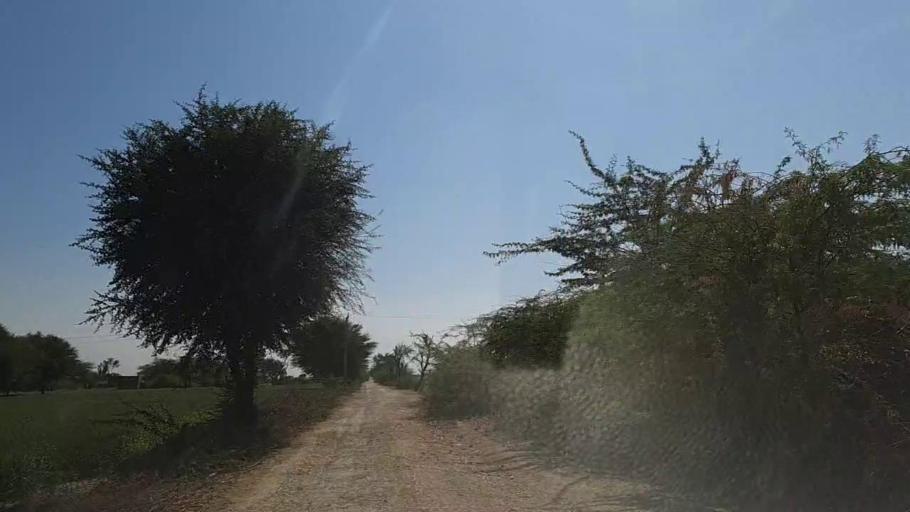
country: PK
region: Sindh
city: Kunri
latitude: 25.2809
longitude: 69.5226
